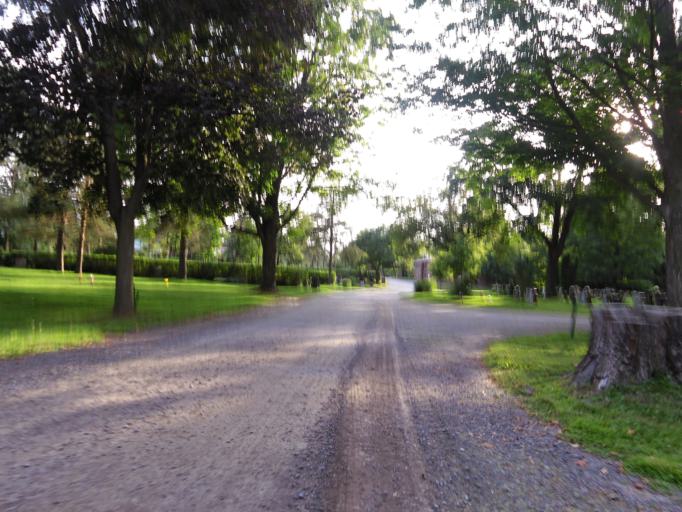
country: CA
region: Ontario
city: Bells Corners
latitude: 45.3404
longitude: -75.7808
